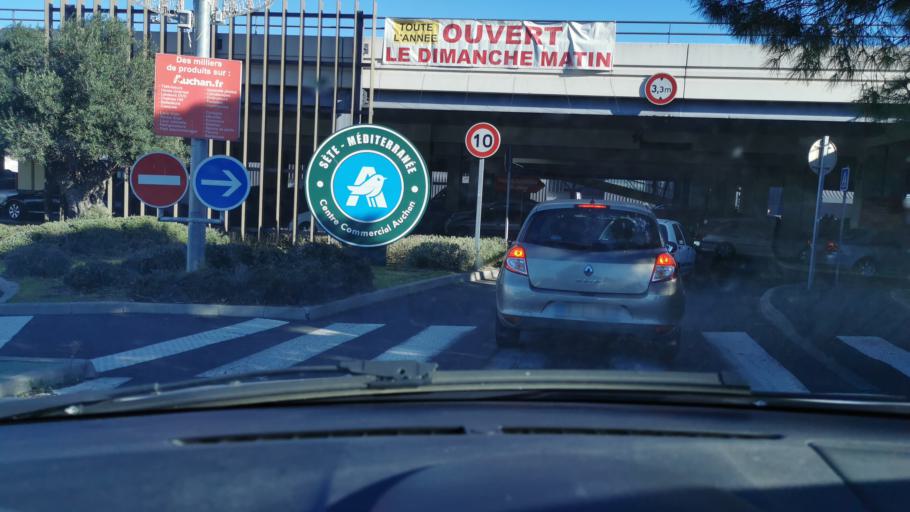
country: FR
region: Languedoc-Roussillon
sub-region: Departement de l'Herault
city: Sete
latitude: 43.4084
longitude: 3.6685
